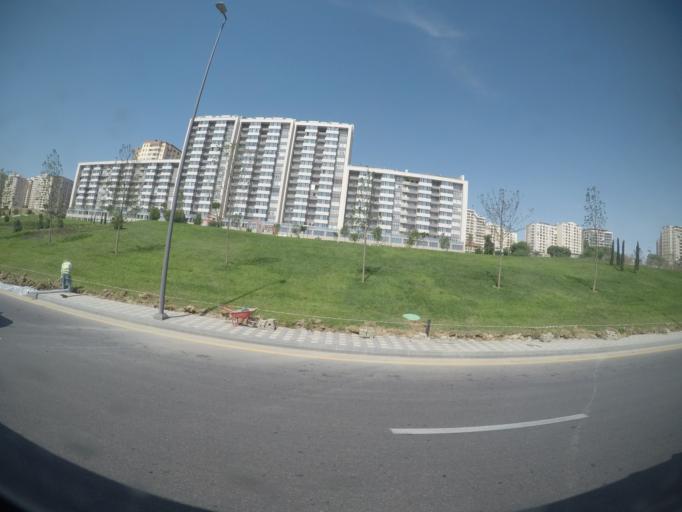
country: AZ
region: Baki
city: Badamdar
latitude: 40.3760
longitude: 49.8252
